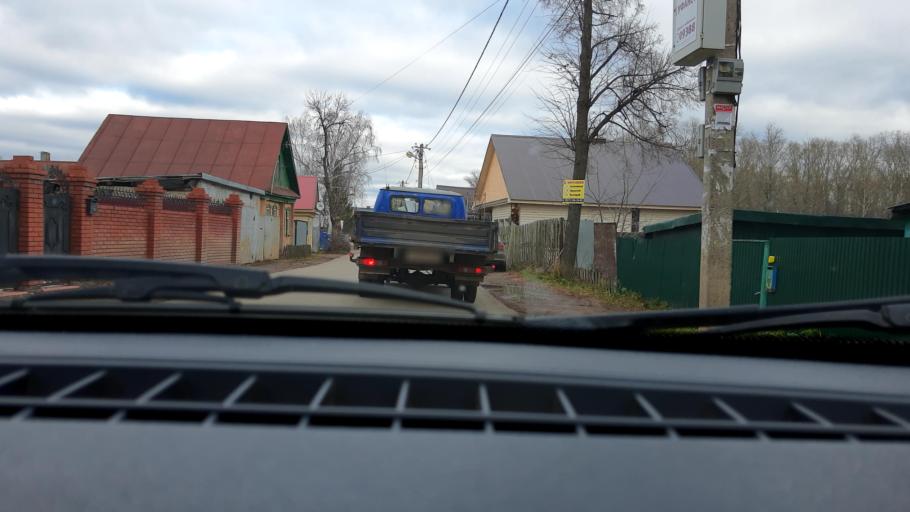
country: RU
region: Bashkortostan
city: Mikhaylovka
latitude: 54.7797
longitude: 55.8934
